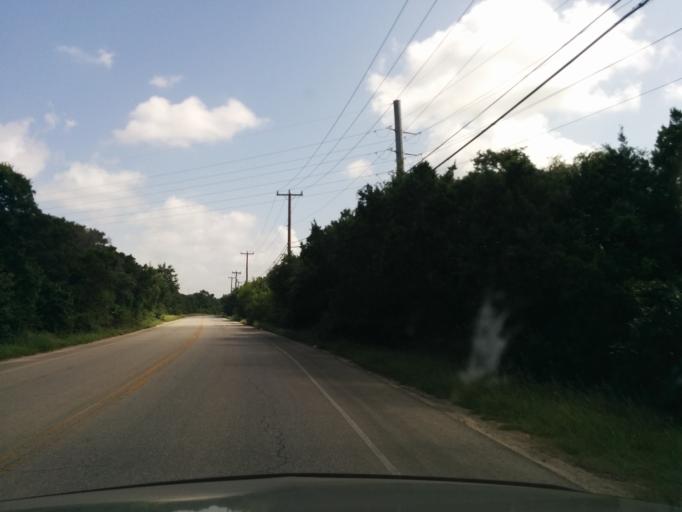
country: US
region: Texas
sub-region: Bexar County
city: Cross Mountain
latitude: 29.5993
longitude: -98.6292
